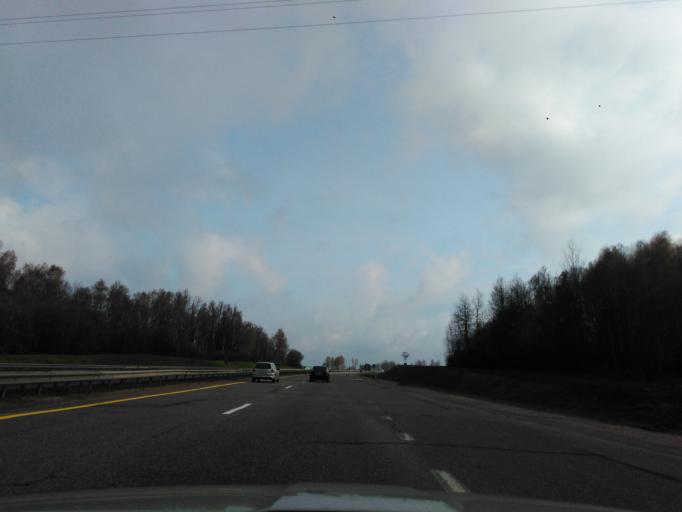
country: BY
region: Minsk
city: Lahoysk
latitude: 54.1725
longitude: 27.8195
